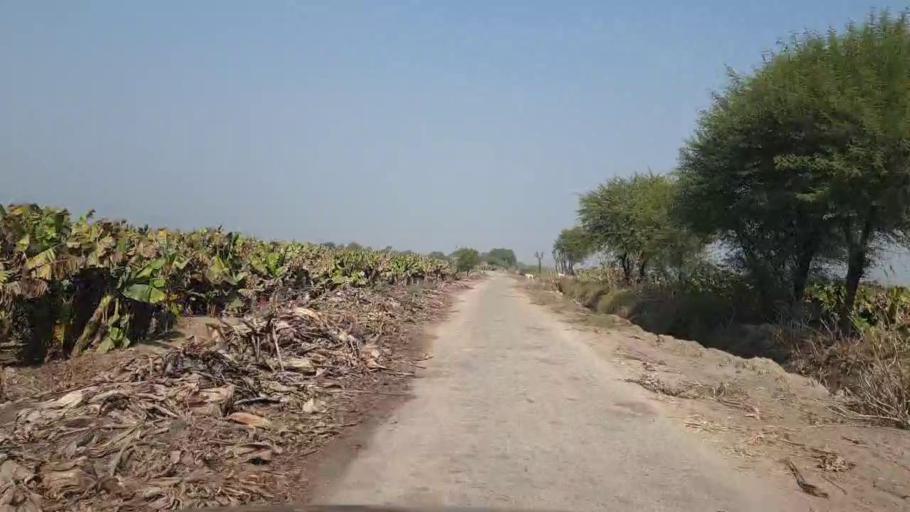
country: PK
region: Sindh
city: Bhit Shah
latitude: 25.7848
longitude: 68.4933
